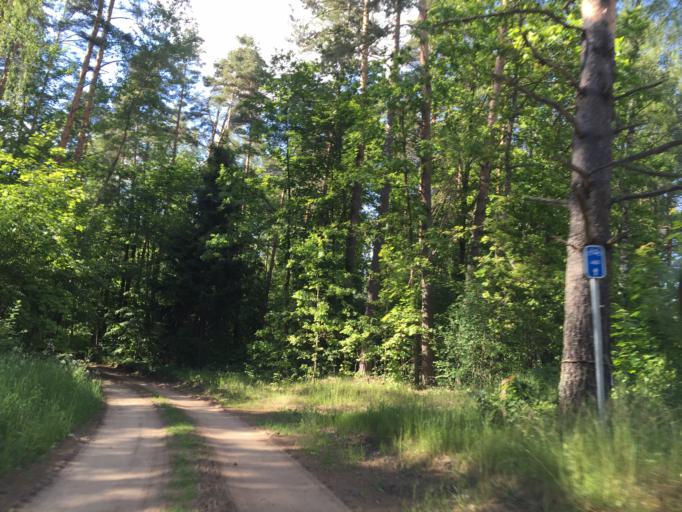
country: LV
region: Vecumnieki
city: Vecumnieki
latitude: 56.4375
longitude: 24.5923
